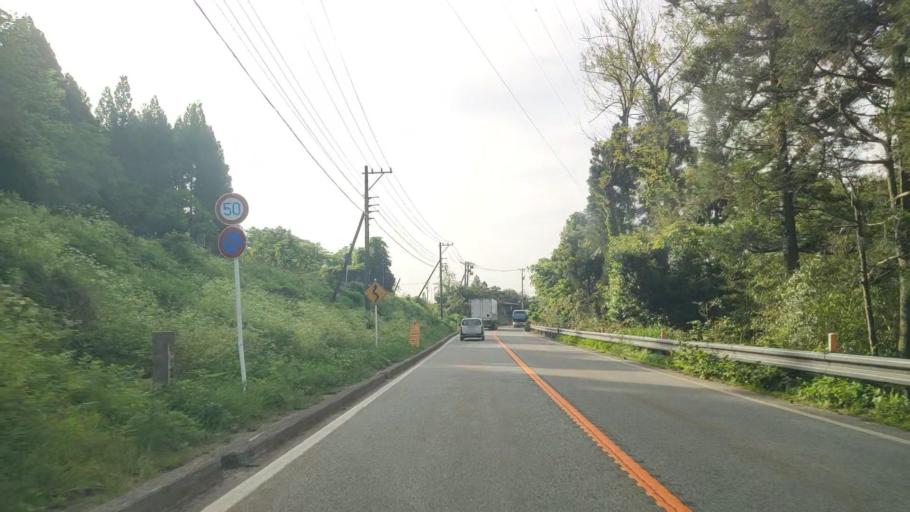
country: JP
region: Toyama
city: Yatsuomachi-higashikumisaka
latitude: 36.5537
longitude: 137.2196
